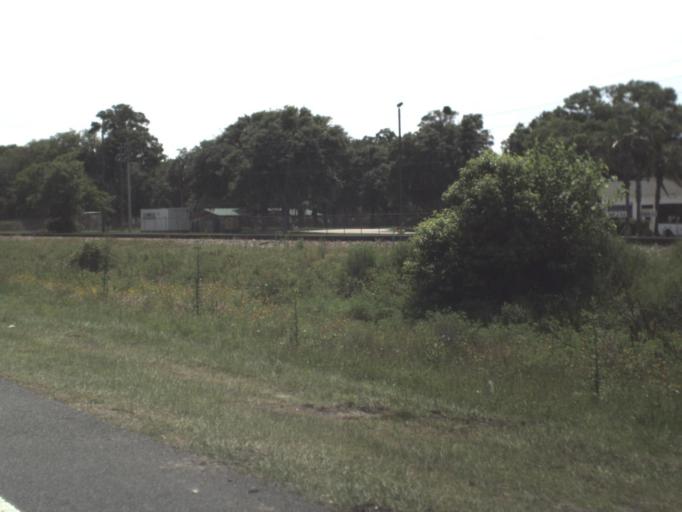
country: US
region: Florida
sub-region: Duval County
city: Jacksonville
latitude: 30.4604
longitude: -81.6350
